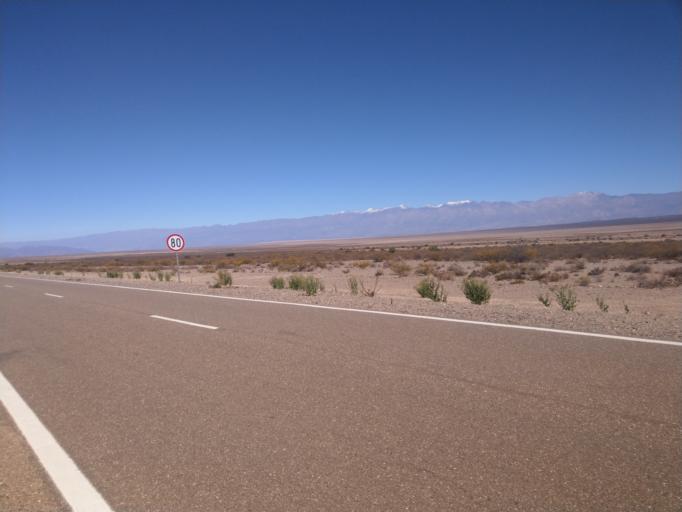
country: AR
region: Catamarca
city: Hualfin
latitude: -27.0640
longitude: -66.5718
